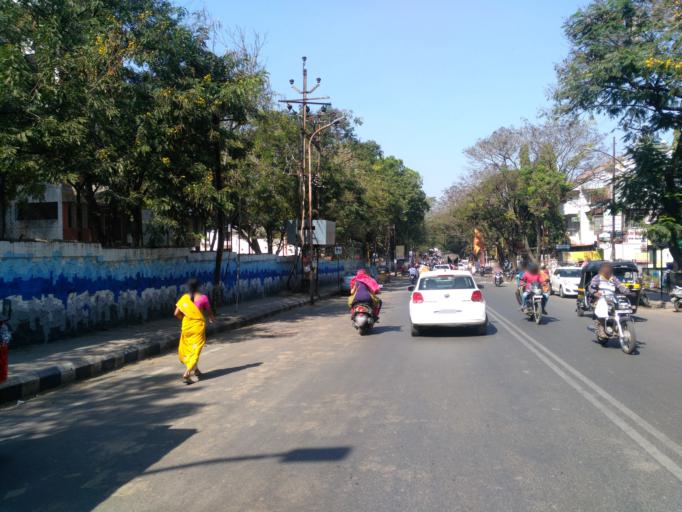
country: IN
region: Maharashtra
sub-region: Pune Division
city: Pune
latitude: 18.4866
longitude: 73.8500
